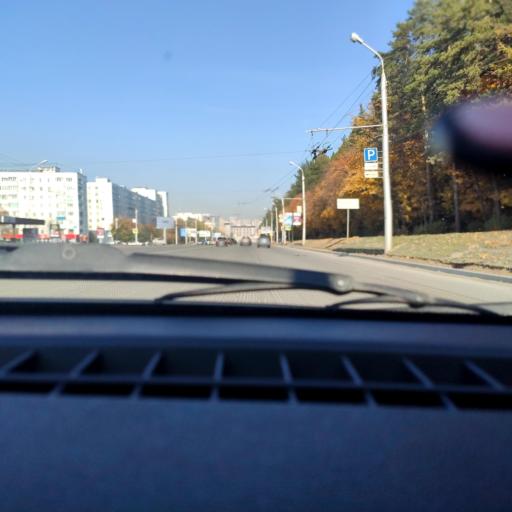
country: RU
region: Bashkortostan
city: Ufa
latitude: 54.7427
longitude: 56.0291
